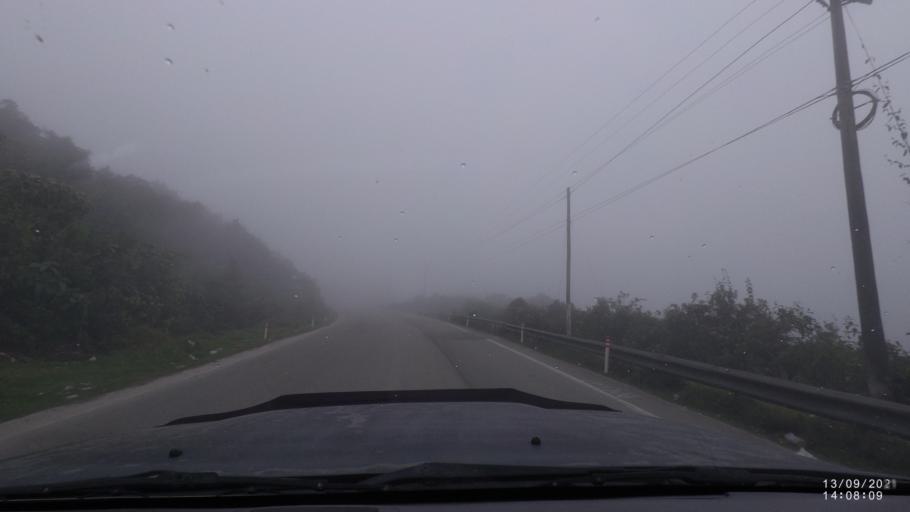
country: BO
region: Cochabamba
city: Colomi
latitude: -17.1726
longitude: -65.8884
